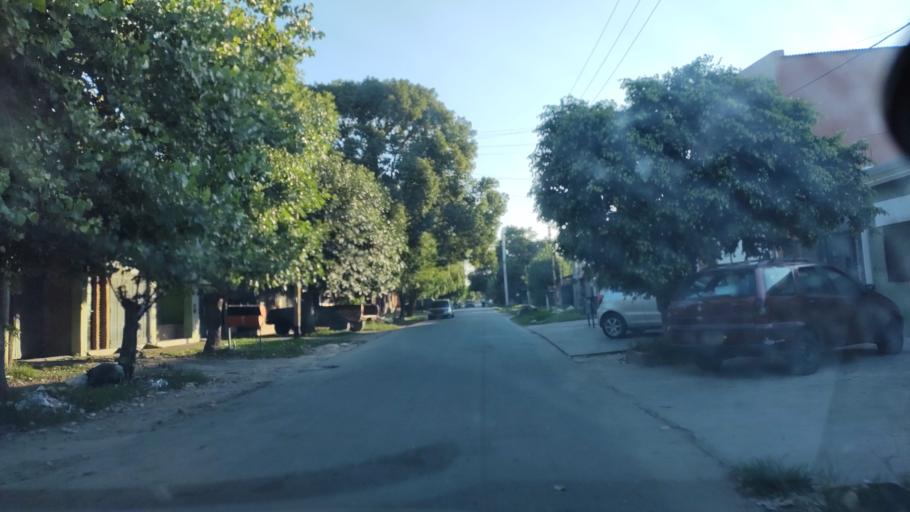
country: AR
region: Buenos Aires
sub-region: Partido de La Plata
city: La Plata
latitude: -34.9694
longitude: -57.9743
